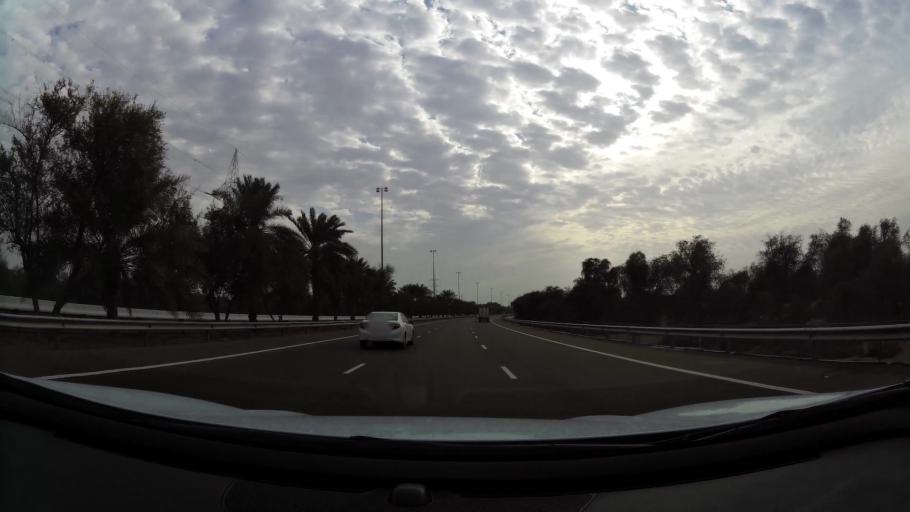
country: AE
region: Abu Dhabi
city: Al Ain
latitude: 24.1719
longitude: 55.2338
